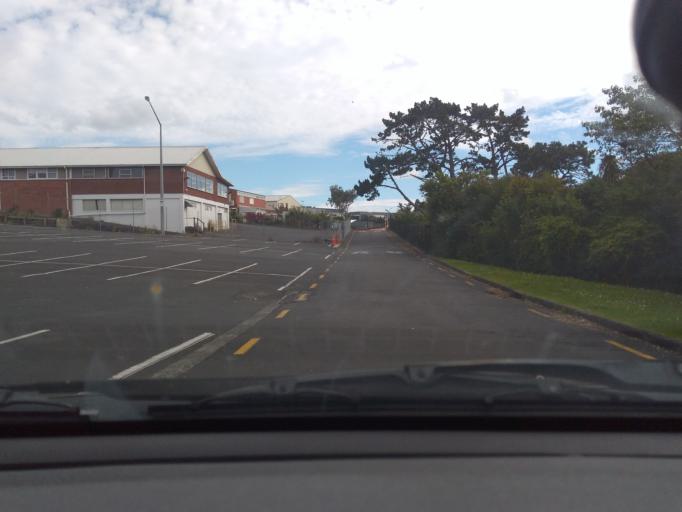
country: NZ
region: Auckland
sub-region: Auckland
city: Waitakere
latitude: -36.9074
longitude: 174.6810
